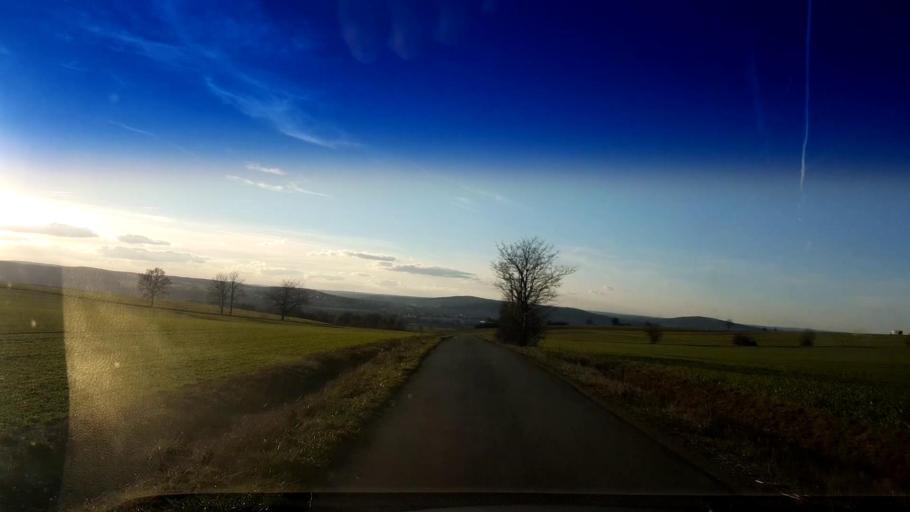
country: DE
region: Bavaria
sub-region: Upper Franconia
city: Buttenheim
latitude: 49.8159
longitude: 11.0358
